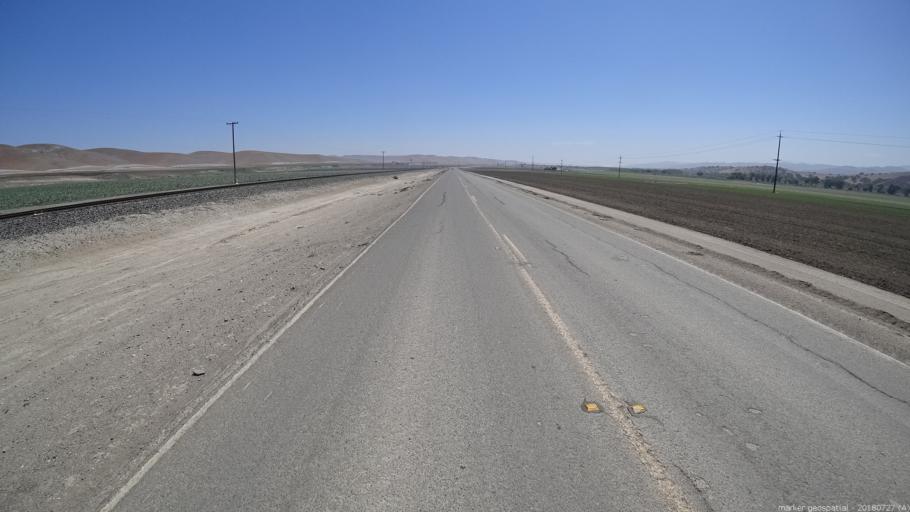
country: US
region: California
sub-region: Monterey County
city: King City
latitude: 36.0937
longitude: -120.9615
